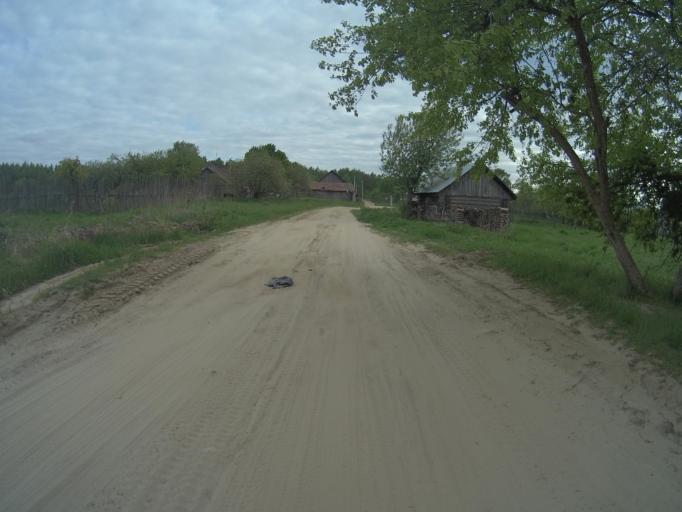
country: RU
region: Vladimir
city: Golovino
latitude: 56.0059
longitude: 40.4423
